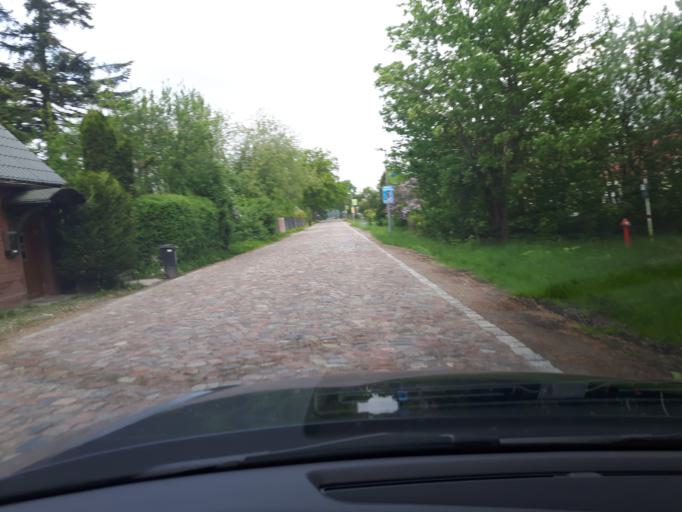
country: DE
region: Mecklenburg-Vorpommern
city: Velgast
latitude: 54.2161
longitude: 12.7342
